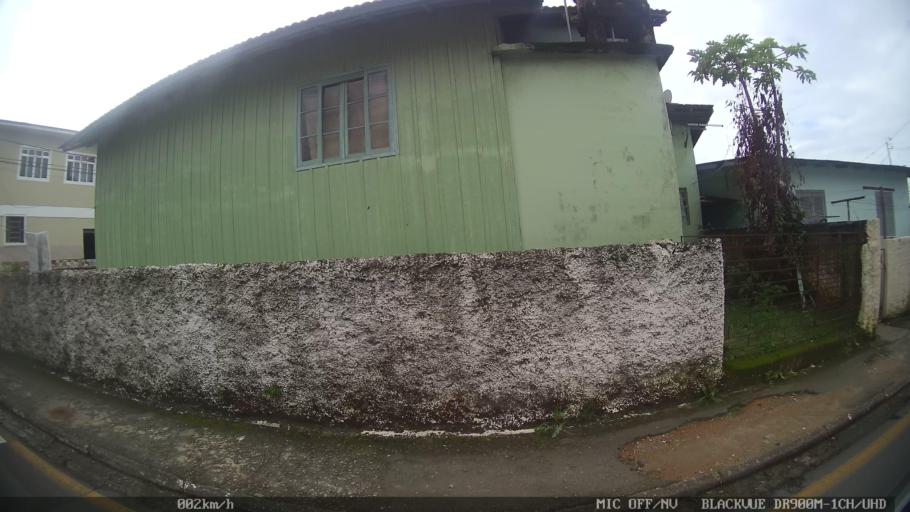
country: BR
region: Santa Catarina
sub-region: Sao Jose
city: Campinas
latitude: -27.5514
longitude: -48.6283
